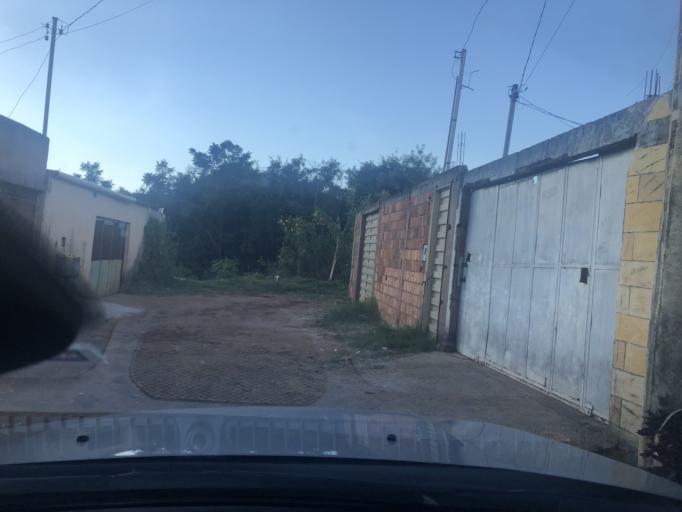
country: BR
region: Federal District
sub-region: Brasilia
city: Brasilia
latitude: -15.8331
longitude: -48.1342
